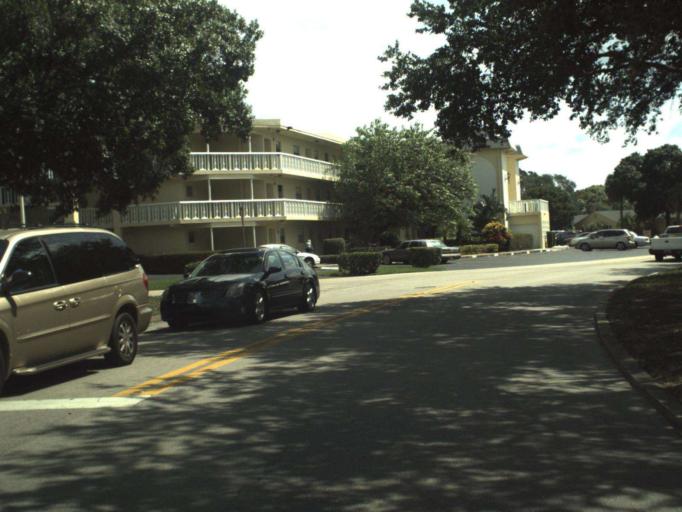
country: US
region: Florida
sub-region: Indian River County
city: Vero Beach
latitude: 27.6400
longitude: -80.3951
